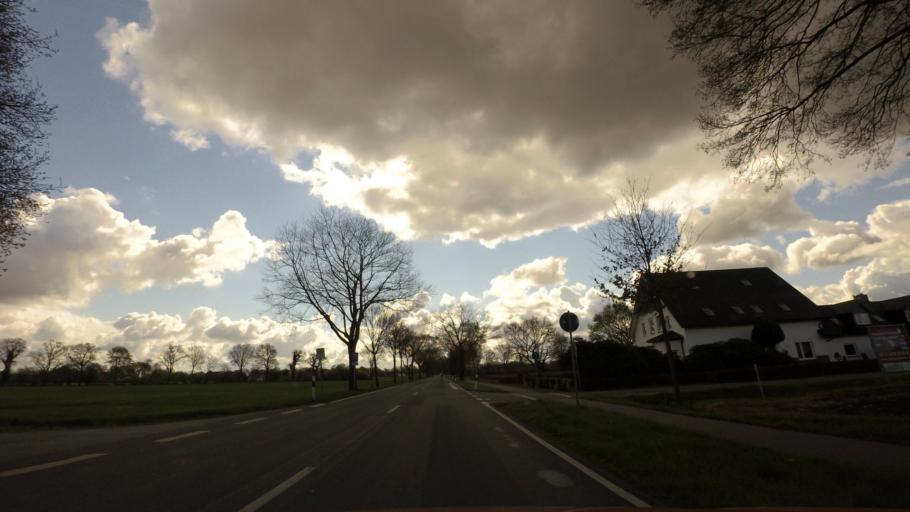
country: DE
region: Lower Saxony
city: Hude
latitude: 53.0526
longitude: 8.4746
